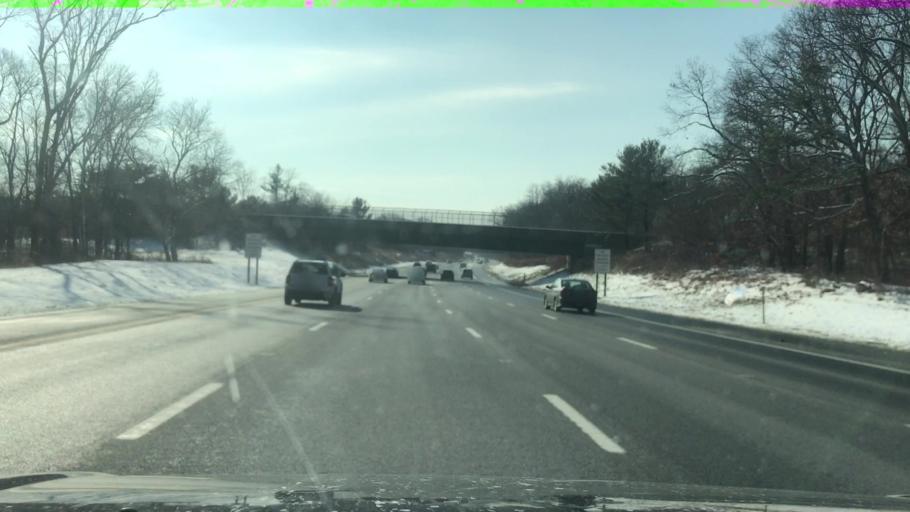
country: US
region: New Jersey
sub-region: Monmouth County
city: Ramtown
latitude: 40.1509
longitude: -74.1065
